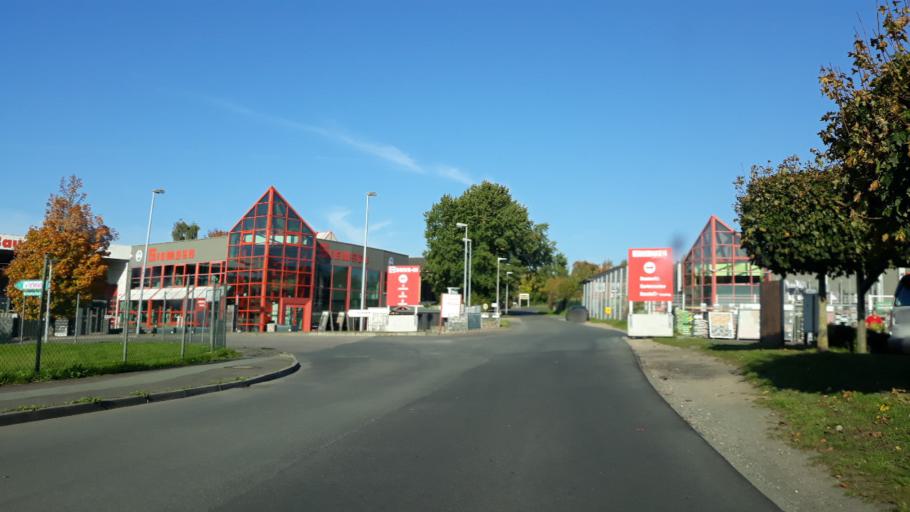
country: DE
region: Schleswig-Holstein
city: Schleswig
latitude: 54.5336
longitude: 9.5567
